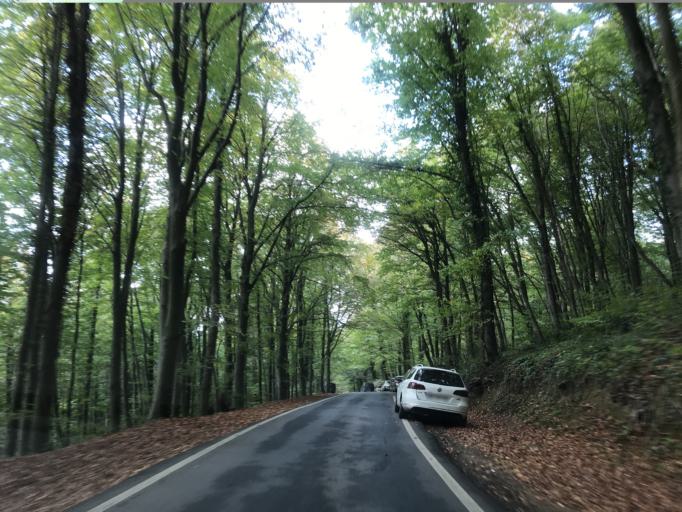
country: TR
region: Istanbul
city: Arikoey
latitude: 41.1877
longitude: 28.9839
